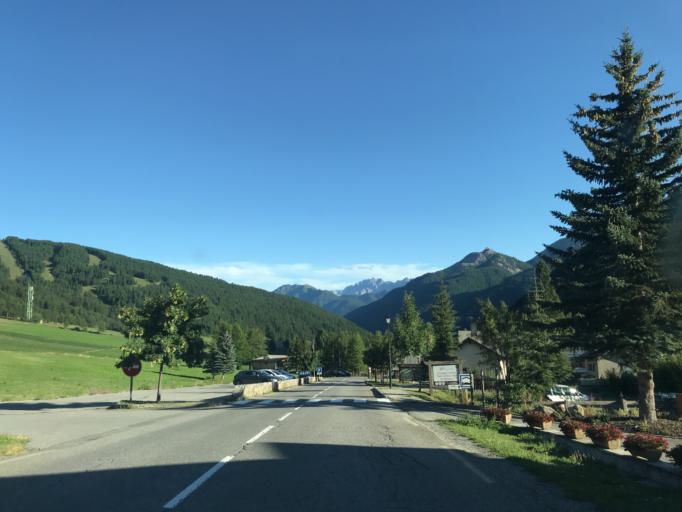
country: FR
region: Provence-Alpes-Cote d'Azur
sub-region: Departement des Hautes-Alpes
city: Villar-Saint-Pancrace
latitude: 44.7929
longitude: 6.7315
